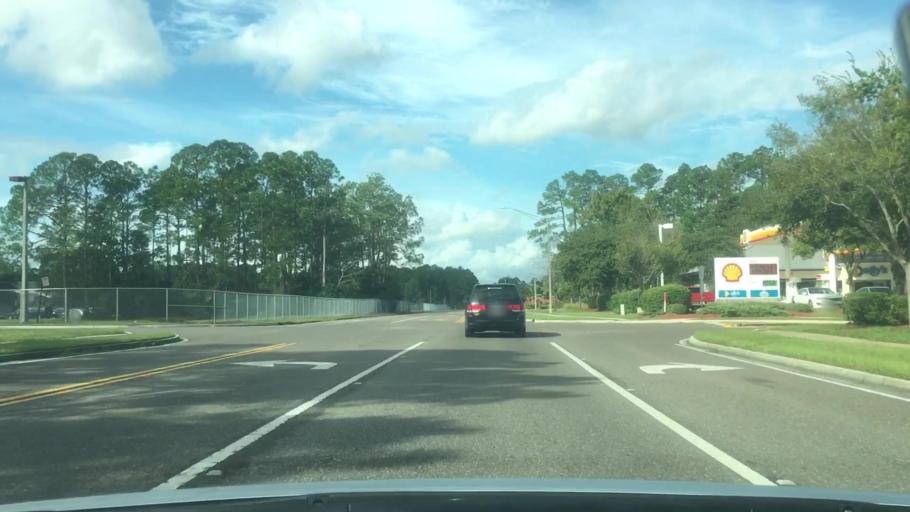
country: US
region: Florida
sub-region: Nassau County
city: Yulee
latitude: 30.4839
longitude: -81.6054
